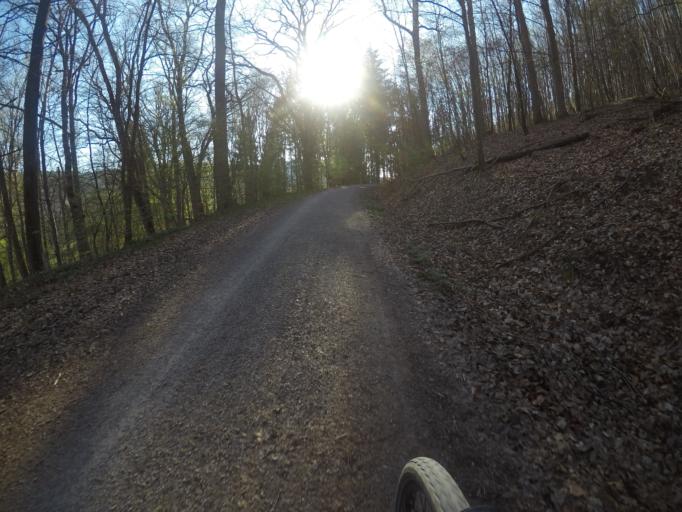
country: DE
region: Baden-Wuerttemberg
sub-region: Regierungsbezirk Stuttgart
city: Filderstadt
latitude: 48.6326
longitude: 9.1857
